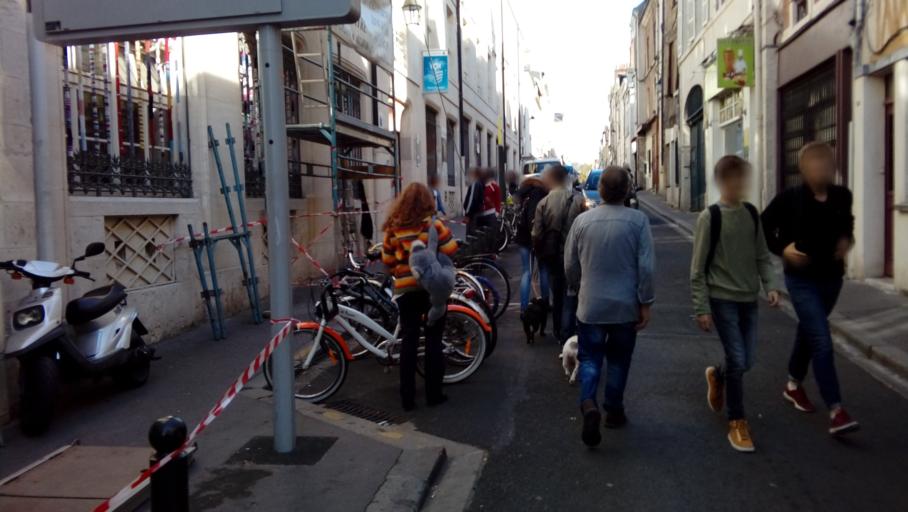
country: FR
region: Centre
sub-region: Departement du Loiret
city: Saint-Jean-le-Blanc
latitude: 47.9004
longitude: 1.9135
